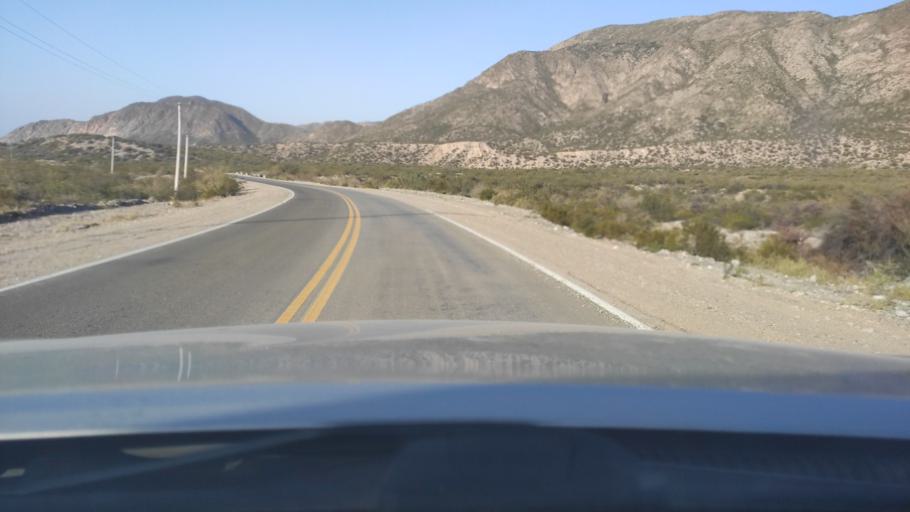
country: AR
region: San Juan
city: Villa Media Agua
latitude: -32.0085
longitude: -68.7716
